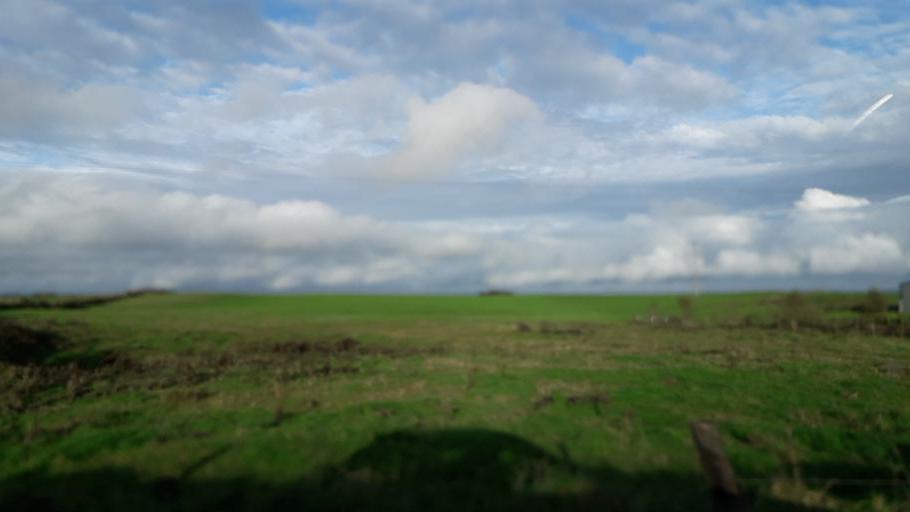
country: IE
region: Connaught
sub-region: Roscommon
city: Boyle
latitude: 53.8034
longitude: -8.3015
